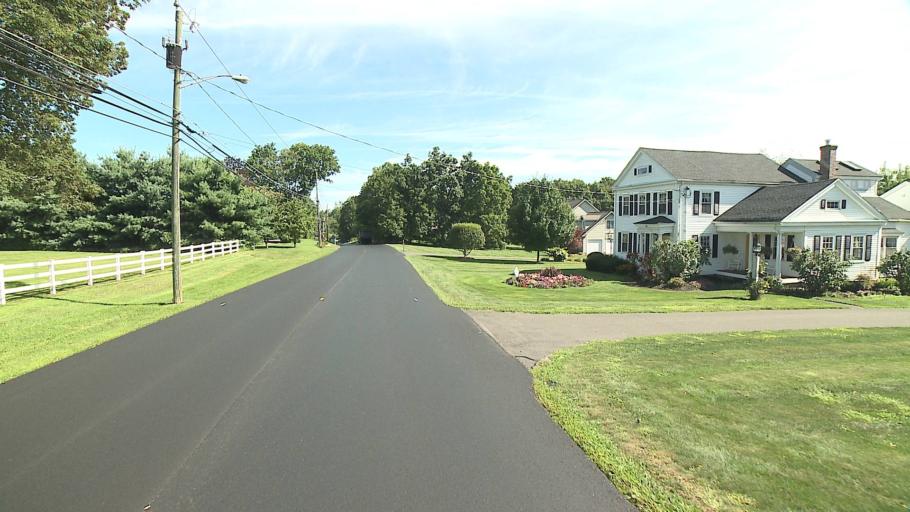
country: US
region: Connecticut
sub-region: Hartford County
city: Tariffville
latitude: 41.9555
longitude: -72.7231
